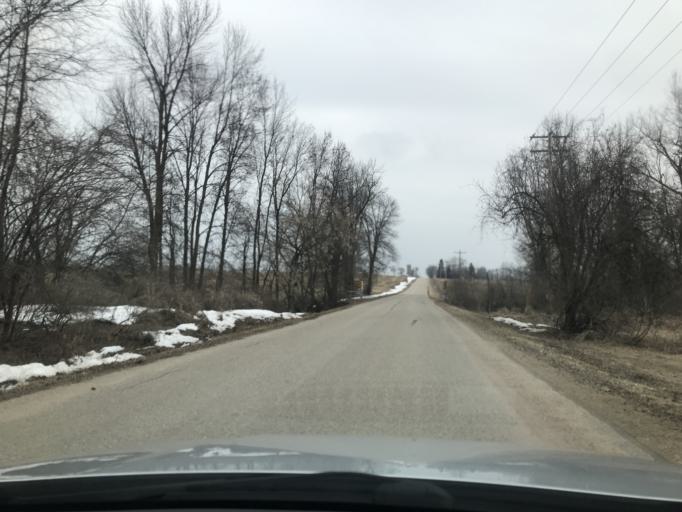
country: US
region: Wisconsin
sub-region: Marinette County
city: Peshtigo
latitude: 45.0491
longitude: -87.8510
